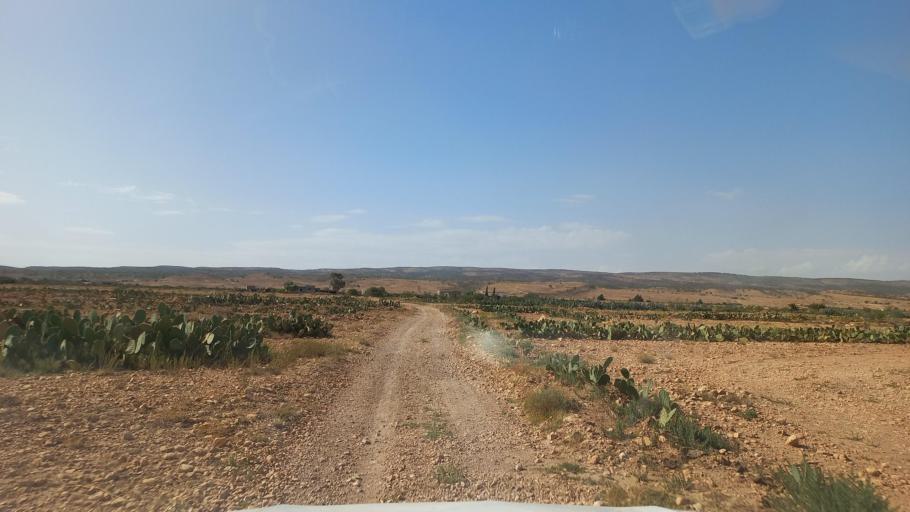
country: TN
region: Al Qasrayn
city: Kasserine
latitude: 35.2853
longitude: 8.9402
